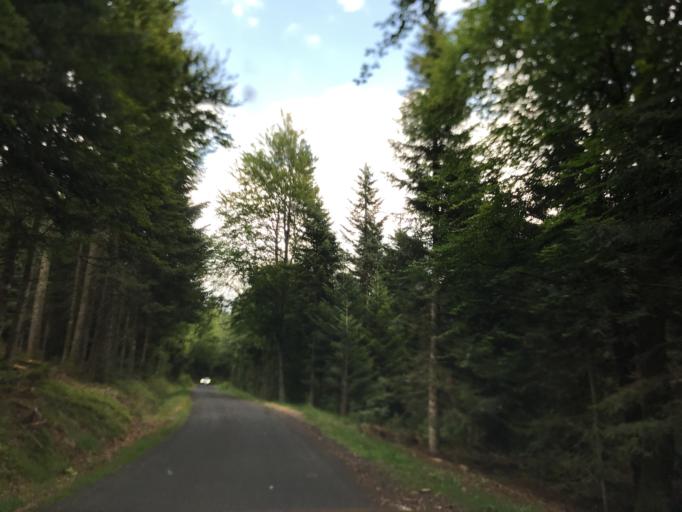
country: FR
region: Rhone-Alpes
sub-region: Departement de la Loire
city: Noiretable
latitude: 45.7628
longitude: 3.7326
